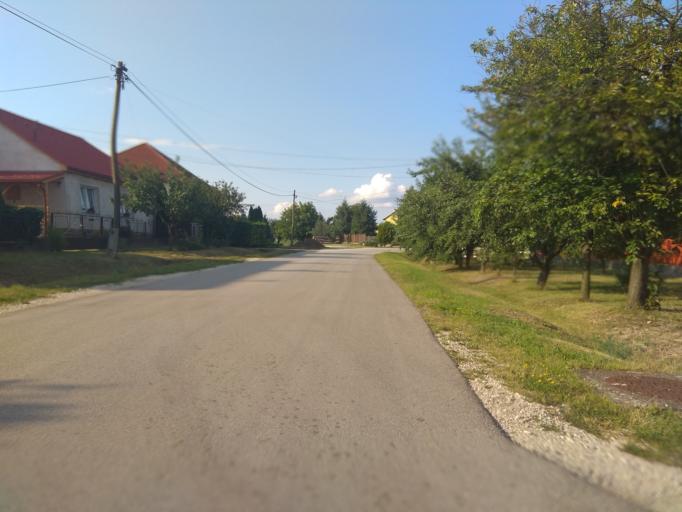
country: HU
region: Borsod-Abauj-Zemplen
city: Emod
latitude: 47.9366
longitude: 20.8081
